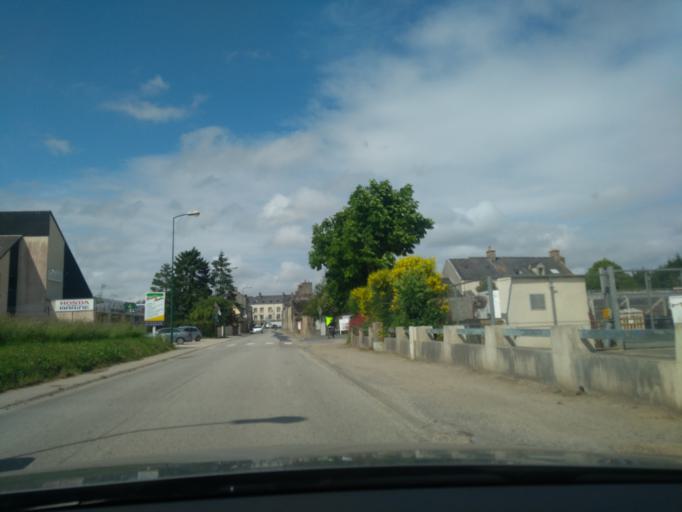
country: FR
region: Lower Normandy
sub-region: Departement de la Manche
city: Quettehou
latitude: 49.5906
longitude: -1.3021
